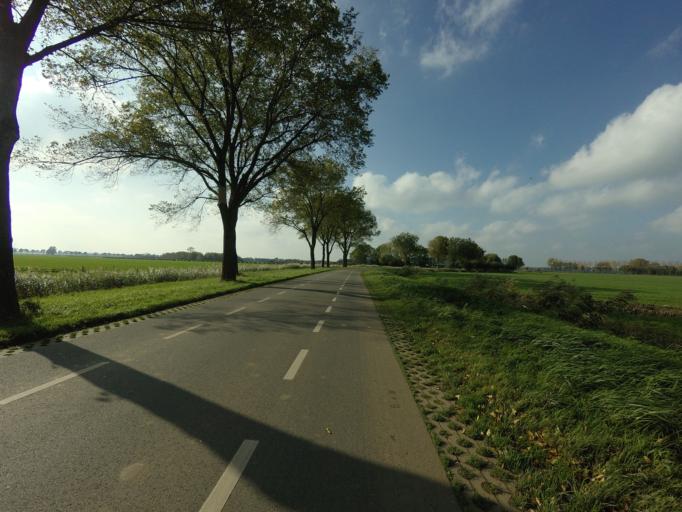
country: NL
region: Gelderland
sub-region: Gemeente Geldermalsen
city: Geldermalsen
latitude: 51.9191
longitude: 5.2918
